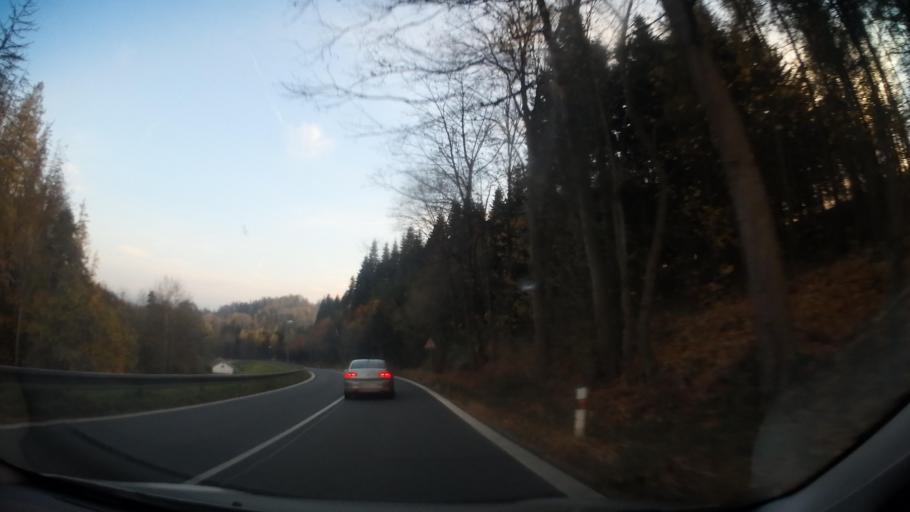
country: CZ
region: Vysocina
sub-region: Okres Pelhrimov
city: Zeliv
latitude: 49.5321
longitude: 15.1670
